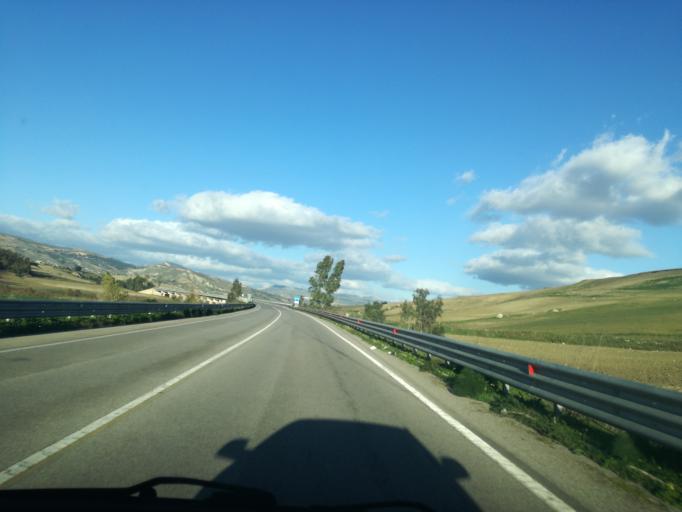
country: IT
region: Sicily
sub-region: Enna
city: Pietraperzia
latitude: 37.4379
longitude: 14.0952
